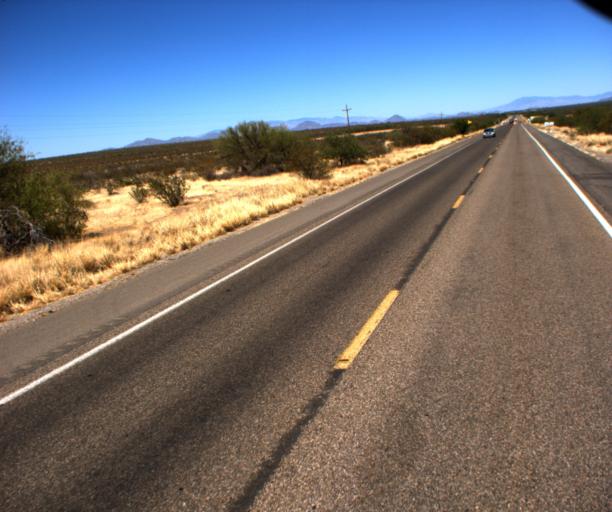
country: US
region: Arizona
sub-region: Pima County
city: Three Points
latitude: 32.0639
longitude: -111.3793
